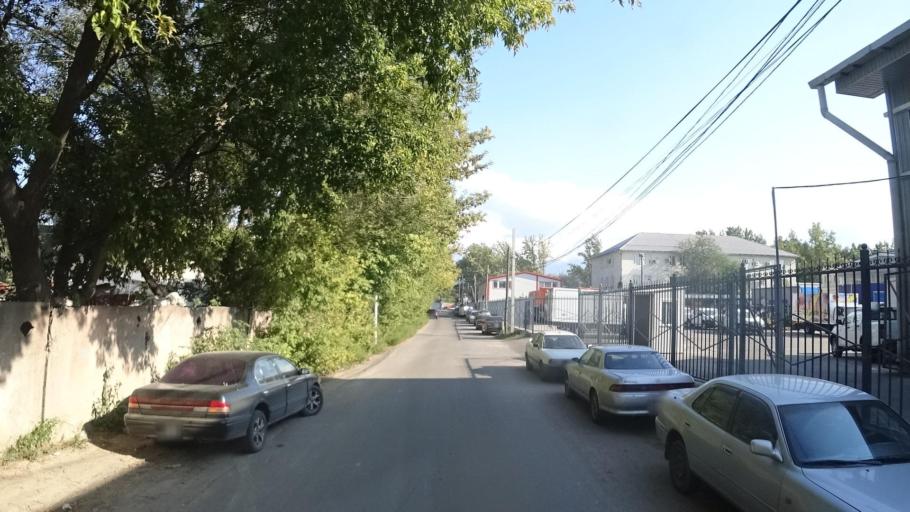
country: KZ
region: Almaty Qalasy
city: Almaty
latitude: 43.2889
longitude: 76.9221
